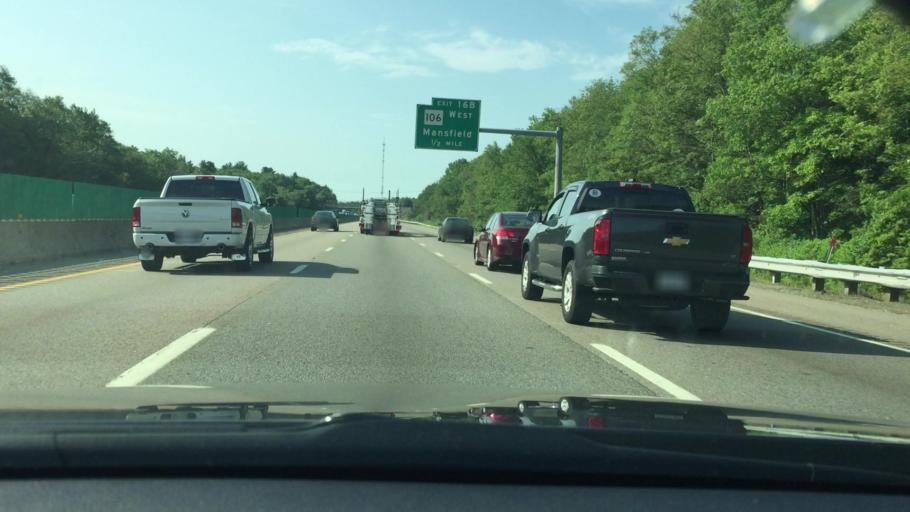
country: US
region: Massachusetts
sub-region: Plymouth County
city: West Bridgewater
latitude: 42.0269
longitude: -71.0498
